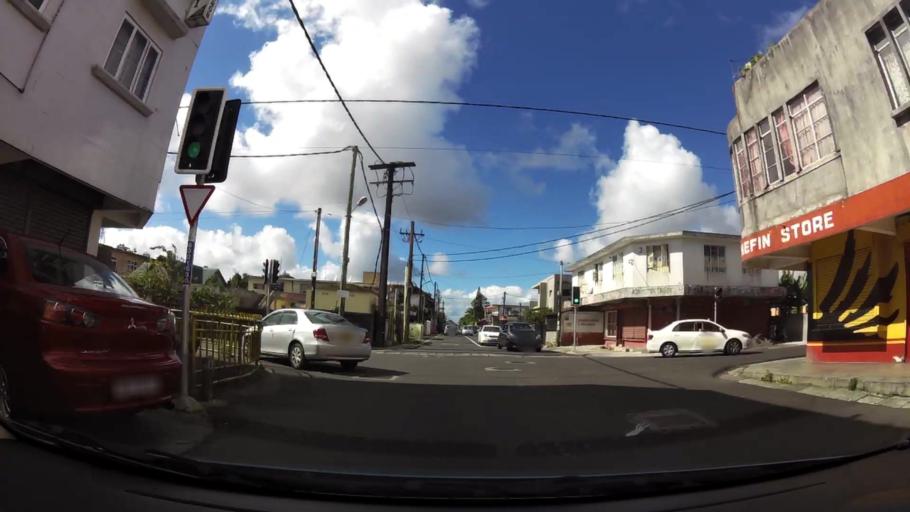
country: MU
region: Plaines Wilhems
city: Curepipe
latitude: -20.3288
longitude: 57.5248
